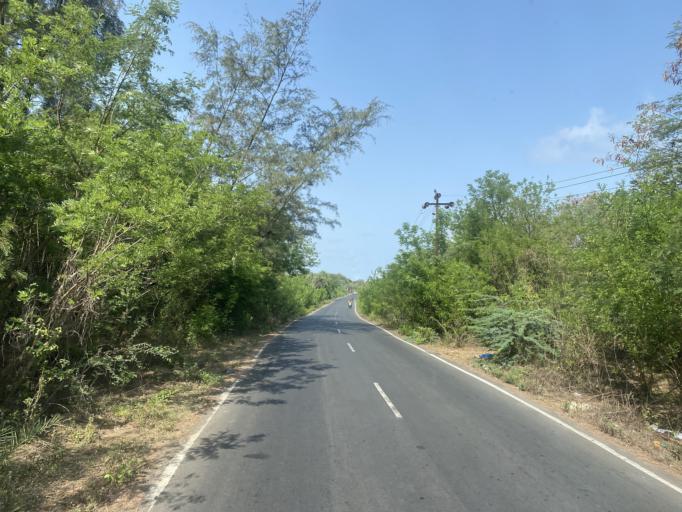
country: IN
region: Daman and Diu
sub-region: Daman District
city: Daman
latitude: 20.3468
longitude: 72.8113
